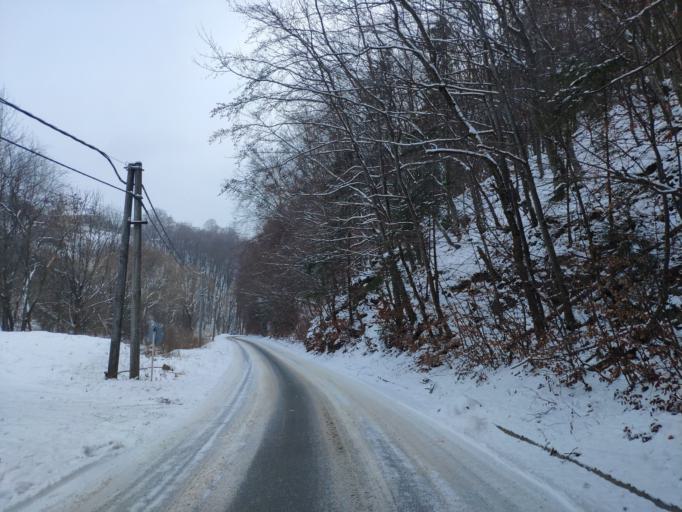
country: SK
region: Kosicky
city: Medzev
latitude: 48.7522
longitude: 21.0029
